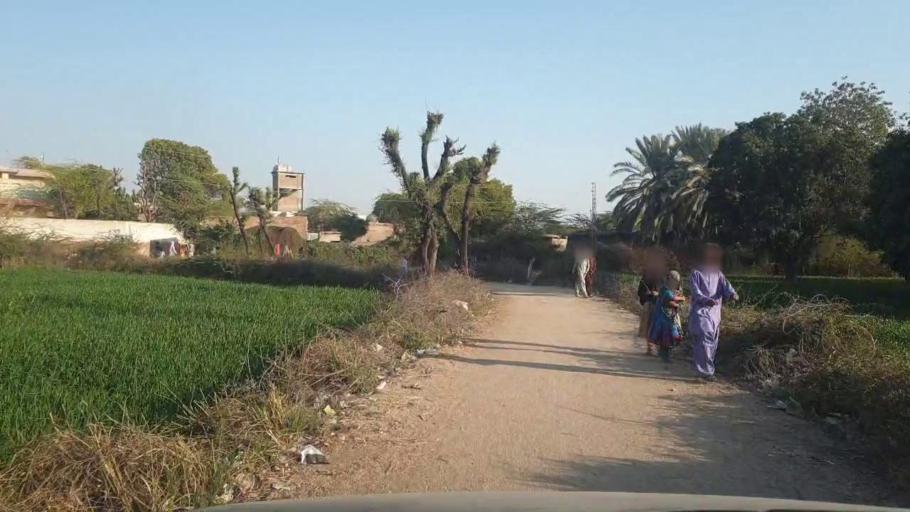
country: PK
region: Sindh
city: Chambar
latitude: 25.2571
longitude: 68.8960
